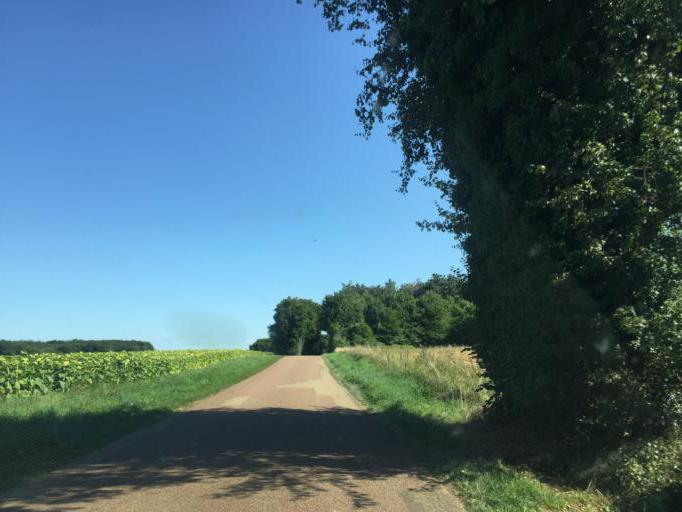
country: FR
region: Bourgogne
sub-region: Departement de l'Yonne
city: Fontenailles
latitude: 47.5375
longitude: 3.3402
